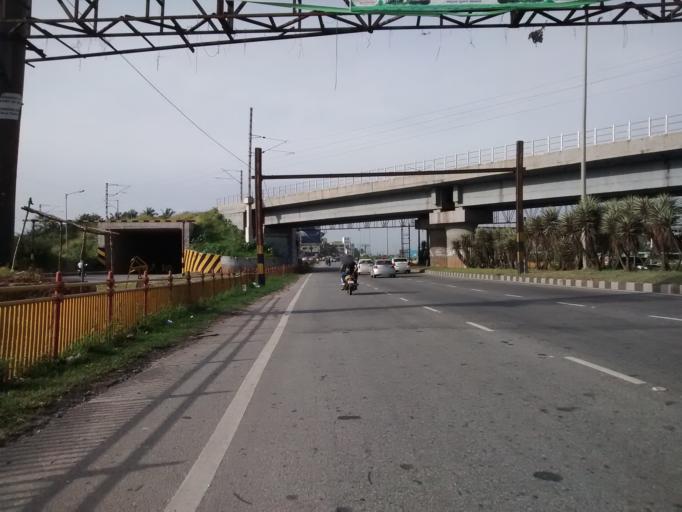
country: IN
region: Karnataka
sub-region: Bangalore Urban
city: Yelahanka
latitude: 13.0923
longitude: 77.5968
